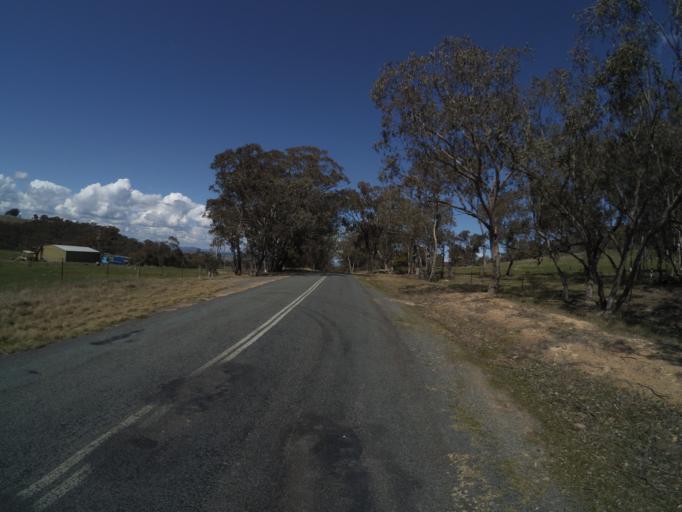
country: AU
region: Australian Capital Territory
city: Macquarie
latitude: -35.2020
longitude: 148.8964
